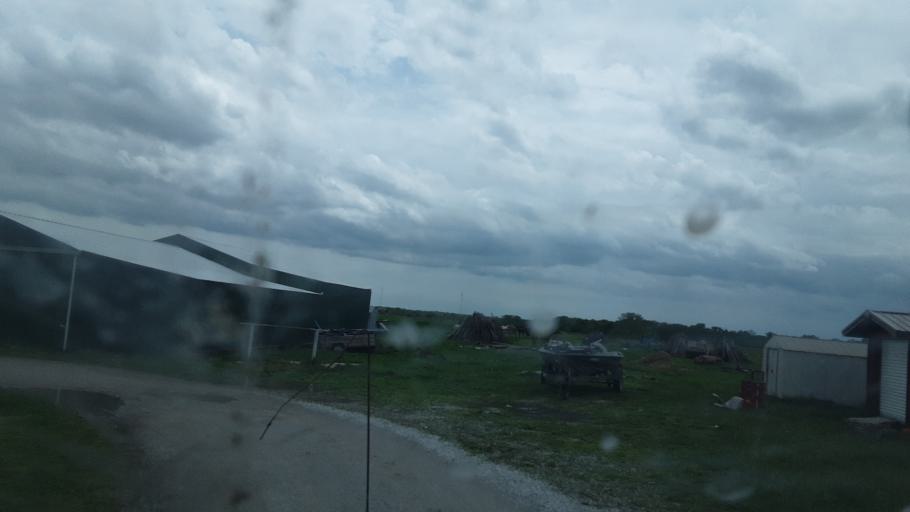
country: US
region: Missouri
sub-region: Clark County
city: Kahoka
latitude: 40.4380
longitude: -91.6056
